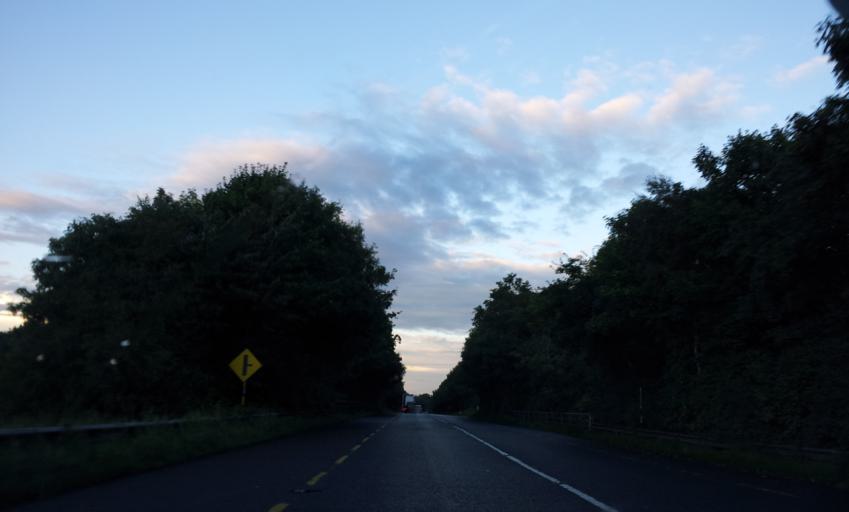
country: IE
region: Munster
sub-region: County Limerick
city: Rathkeale
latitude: 52.5294
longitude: -8.9354
